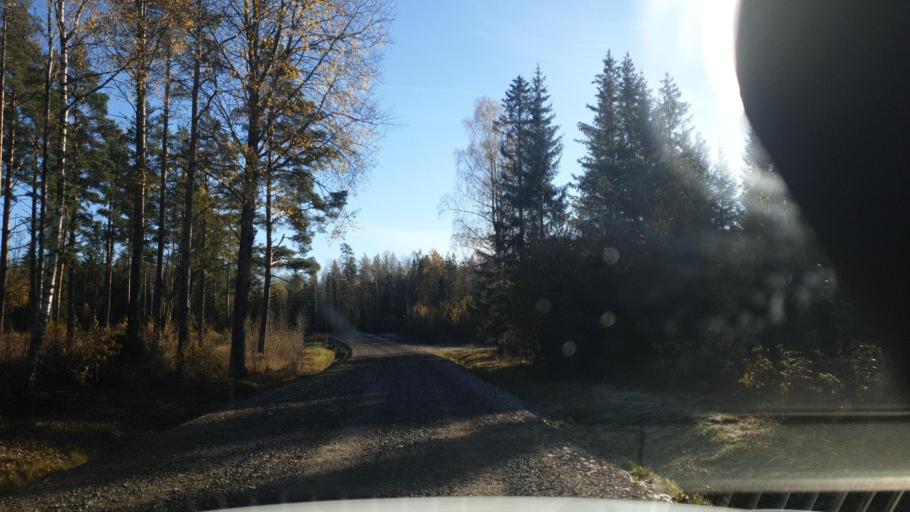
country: SE
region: Vaermland
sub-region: Karlstads Kommun
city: Valberg
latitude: 59.4166
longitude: 13.1243
